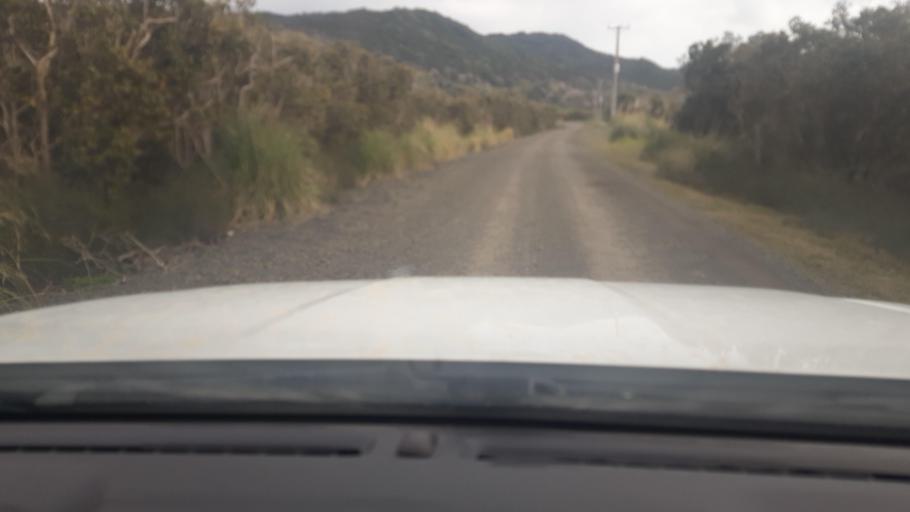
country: NZ
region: Northland
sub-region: Far North District
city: Ahipara
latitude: -35.2582
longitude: 173.2075
